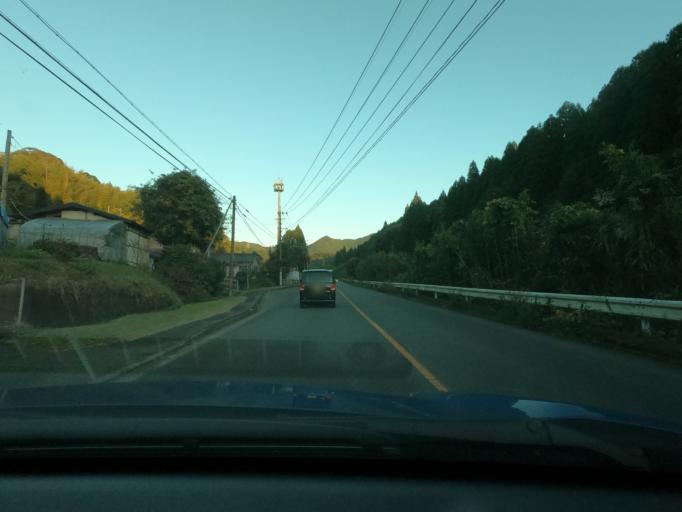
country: JP
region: Kagoshima
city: Satsumasendai
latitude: 31.7963
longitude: 130.4751
